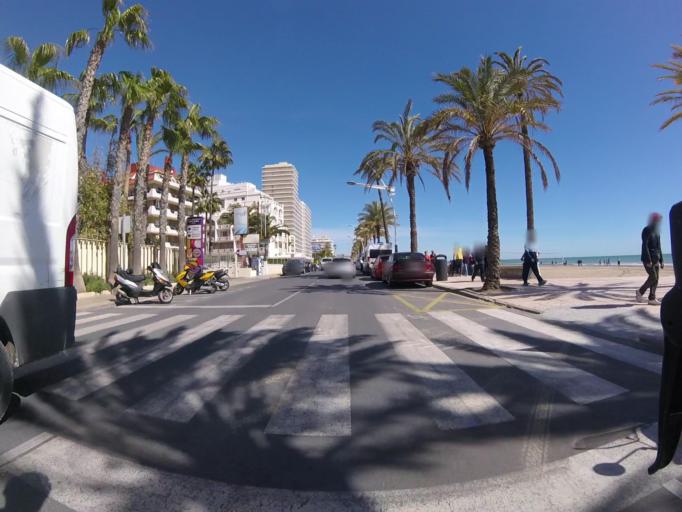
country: ES
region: Valencia
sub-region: Provincia de Castello
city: Peniscola
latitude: 40.3641
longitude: 0.4029
